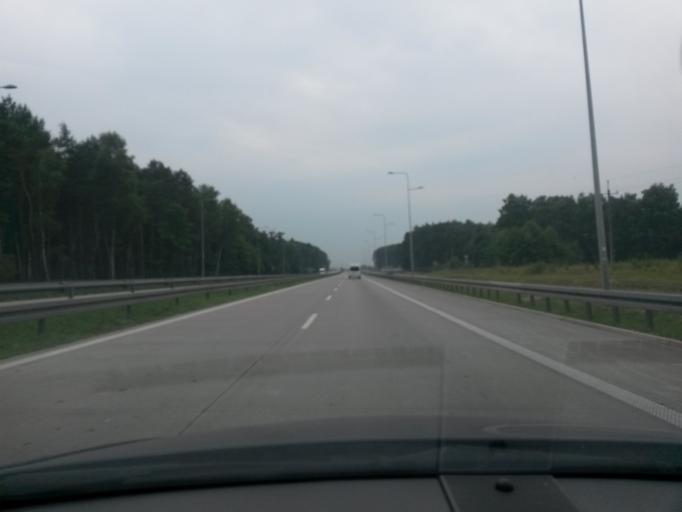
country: PL
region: Lodz Voivodeship
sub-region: Powiat piotrkowski
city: Wolborz
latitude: 51.4909
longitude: 19.8280
